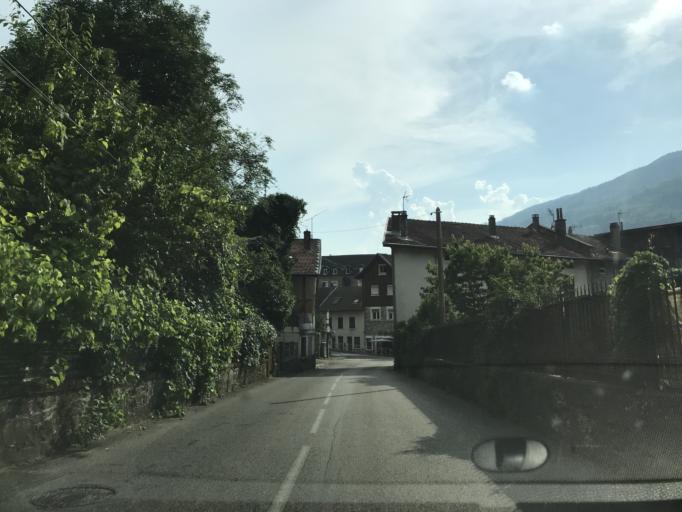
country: FR
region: Rhone-Alpes
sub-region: Departement de l'Isere
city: Allevard
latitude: 45.3937
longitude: 6.0769
